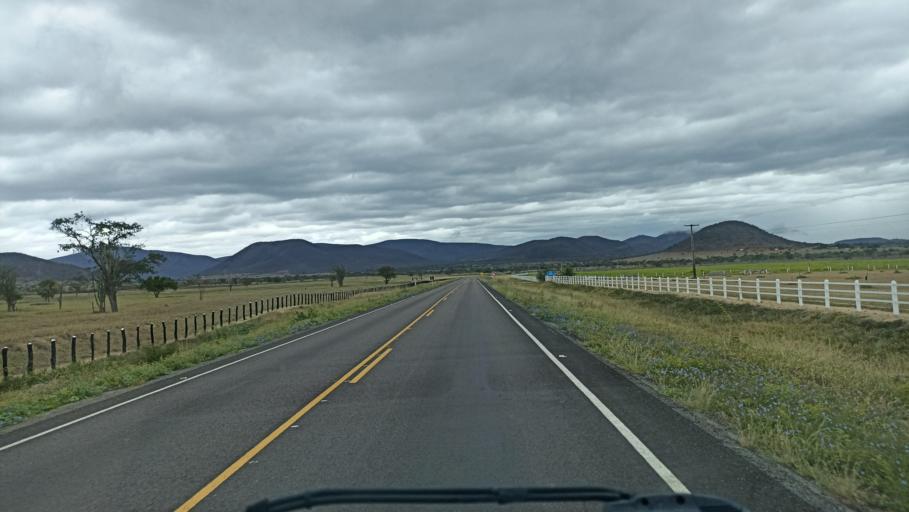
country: BR
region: Bahia
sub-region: Iacu
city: Iacu
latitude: -12.9181
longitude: -40.4129
